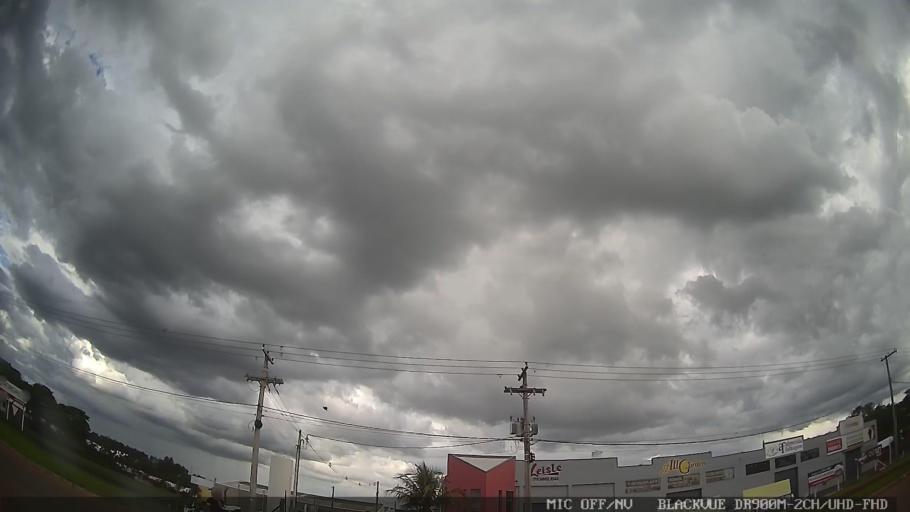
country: BR
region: Sao Paulo
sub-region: Jaguariuna
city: Jaguariuna
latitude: -22.6243
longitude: -47.0192
